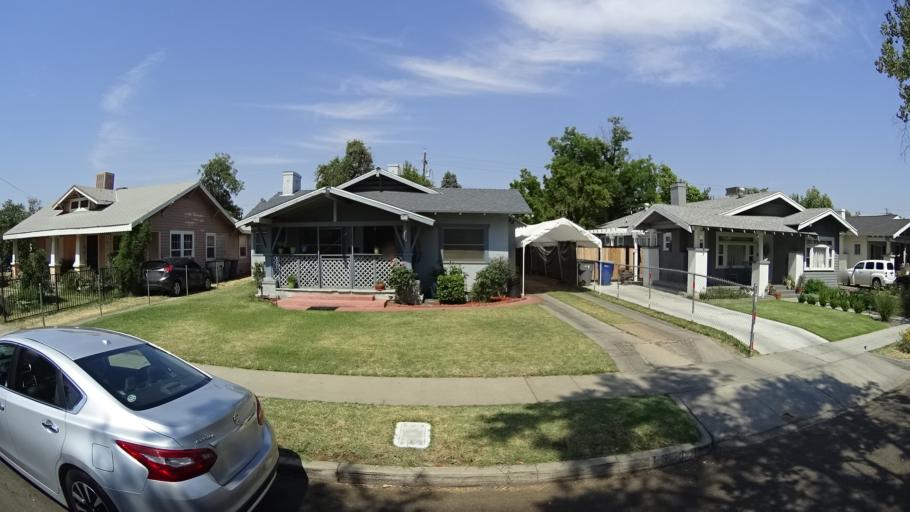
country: US
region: California
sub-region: Fresno County
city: Fresno
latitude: 36.7606
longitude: -119.7967
